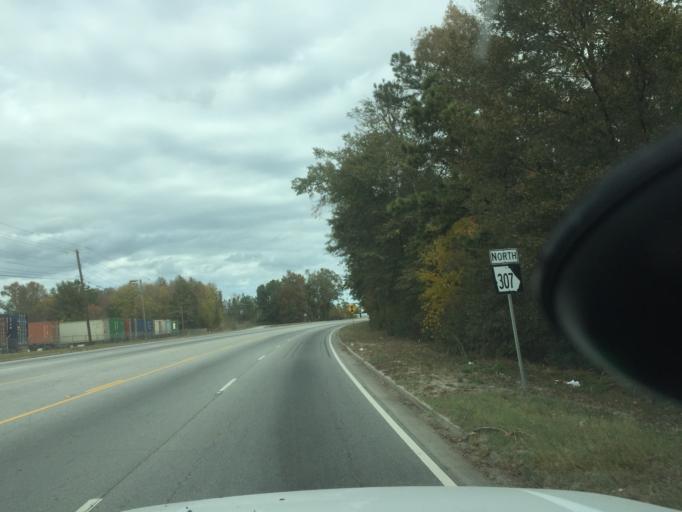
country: US
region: Georgia
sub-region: Chatham County
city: Garden City
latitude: 32.1085
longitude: -81.1956
